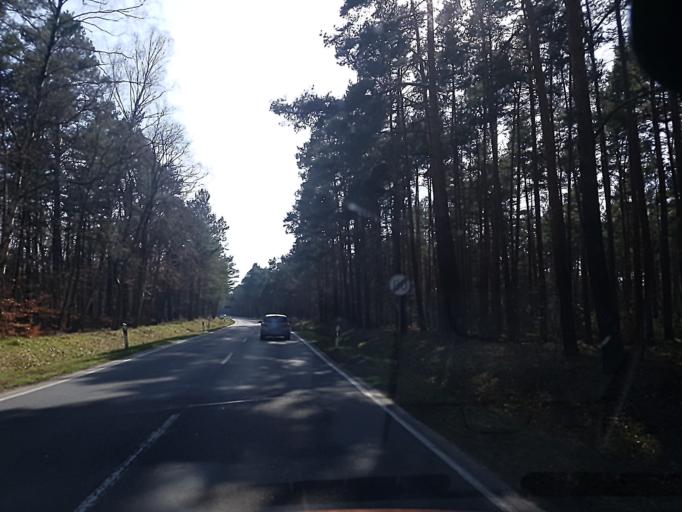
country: DE
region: Brandenburg
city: Calau
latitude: 51.7203
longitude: 13.9264
